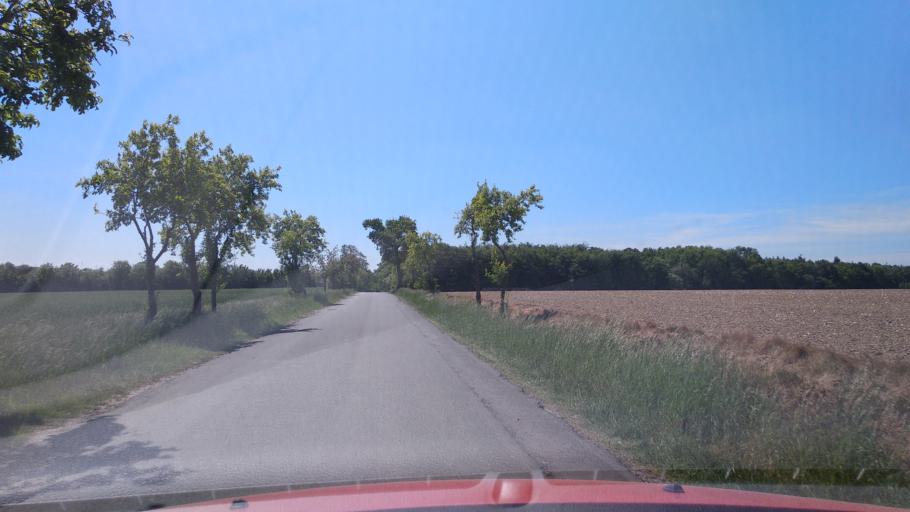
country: DE
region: North Rhine-Westphalia
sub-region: Regierungsbezirk Detmold
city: Paderborn
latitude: 51.6742
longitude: 8.7683
